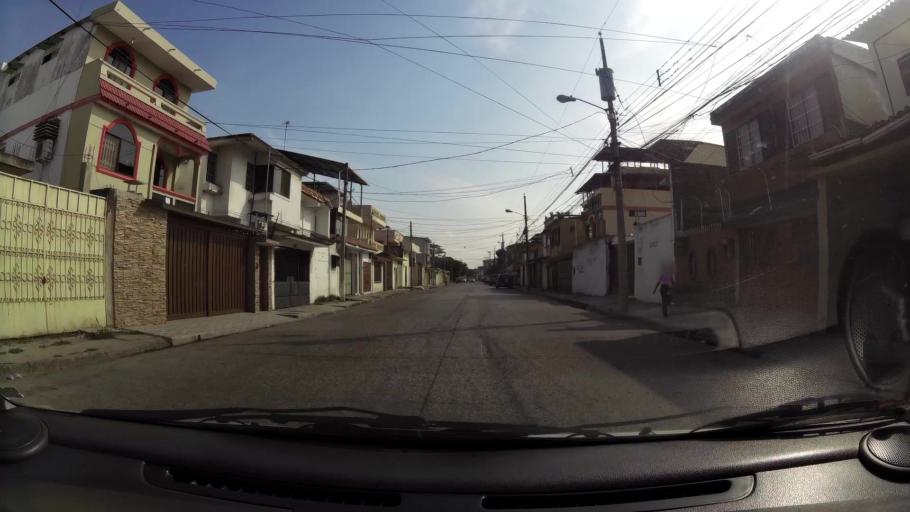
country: EC
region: Guayas
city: Guayaquil
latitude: -2.1877
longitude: -79.9103
